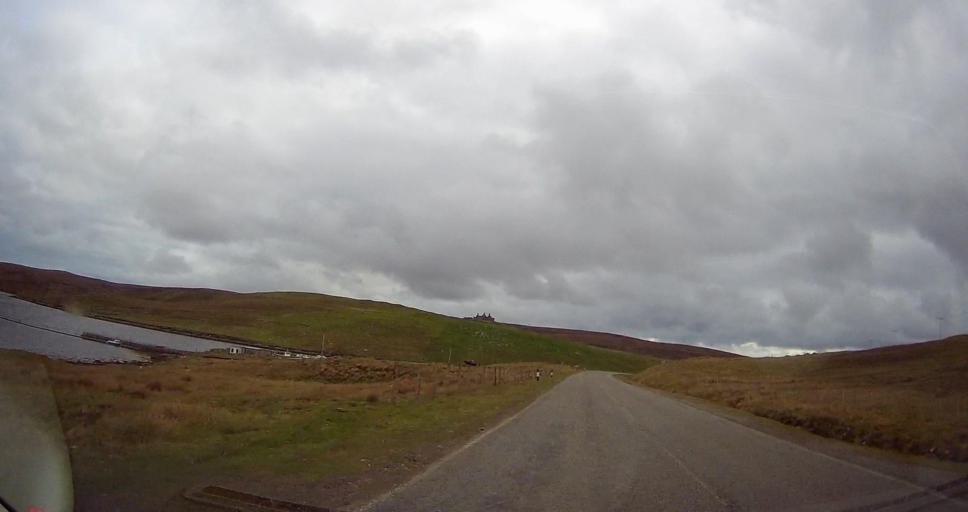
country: GB
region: Scotland
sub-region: Shetland Islands
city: Shetland
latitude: 60.6038
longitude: -1.1185
